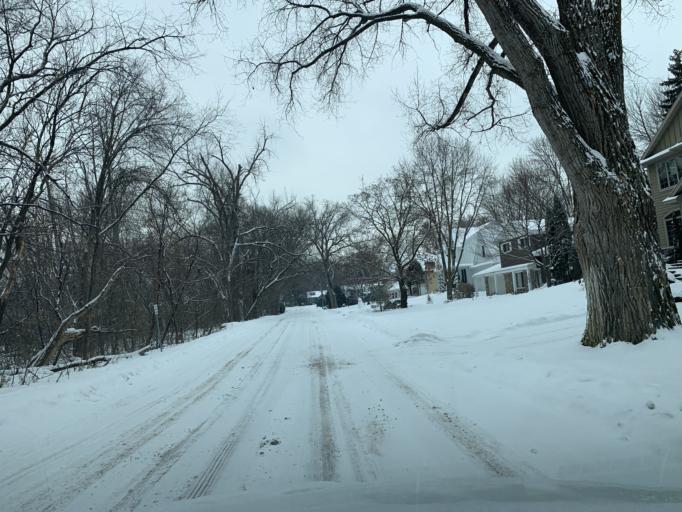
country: US
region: Minnesota
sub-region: Hennepin County
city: Saint Louis Park
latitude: 44.9288
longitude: -93.3368
